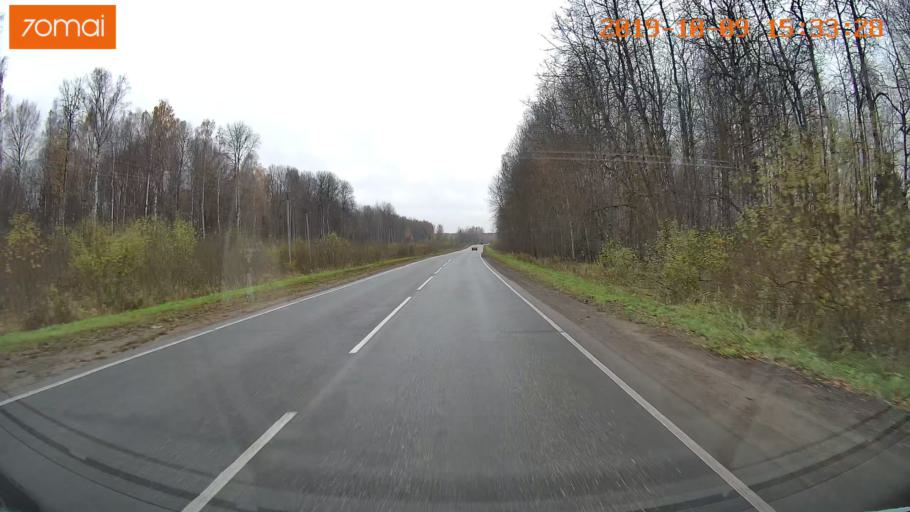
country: RU
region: Kostroma
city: Oktyabr'skiy
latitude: 57.9514
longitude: 41.2622
